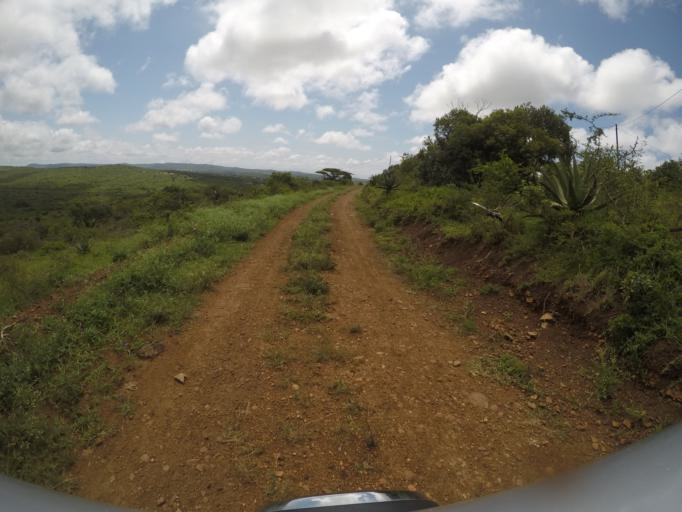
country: ZA
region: KwaZulu-Natal
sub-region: uThungulu District Municipality
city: Empangeni
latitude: -28.5774
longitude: 31.8275
